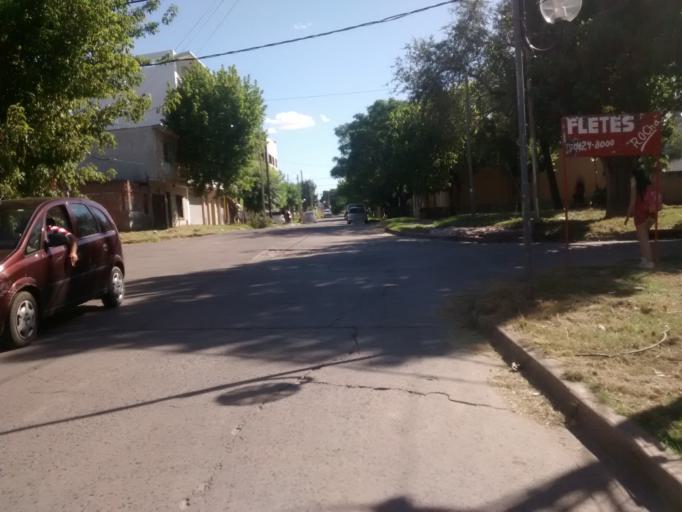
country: AR
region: Buenos Aires
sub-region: Partido de La Plata
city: La Plata
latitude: -34.9115
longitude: -57.9230
